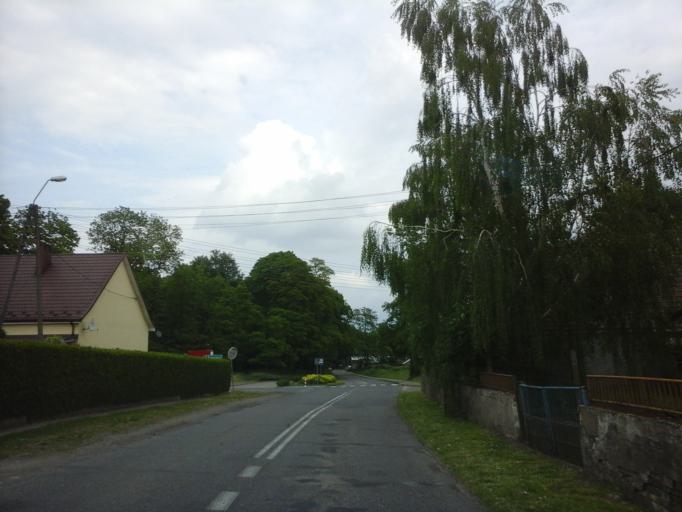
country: PL
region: West Pomeranian Voivodeship
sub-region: Powiat choszczenski
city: Pelczyce
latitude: 53.0900
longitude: 15.2986
